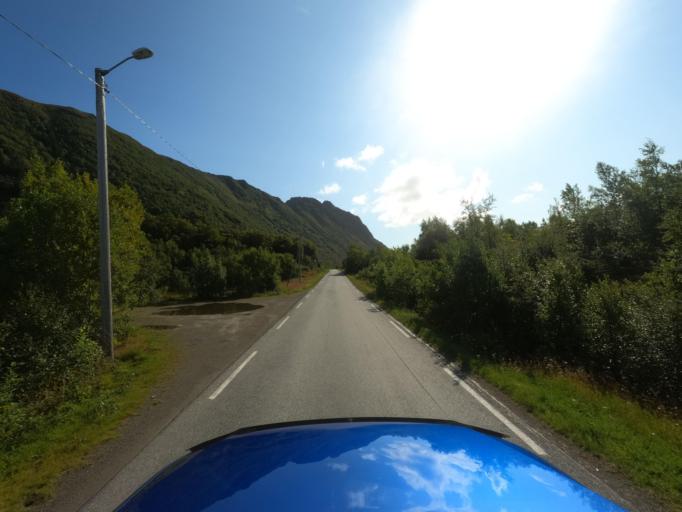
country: NO
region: Nordland
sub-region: Vestvagoy
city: Evjen
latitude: 68.1416
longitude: 13.7736
